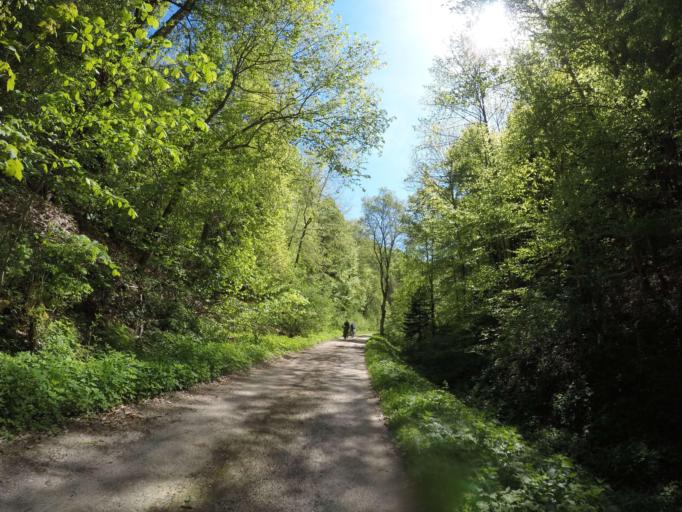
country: DE
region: Baden-Wuerttemberg
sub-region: Tuebingen Region
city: Schelklingen
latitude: 48.4046
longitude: 9.7305
